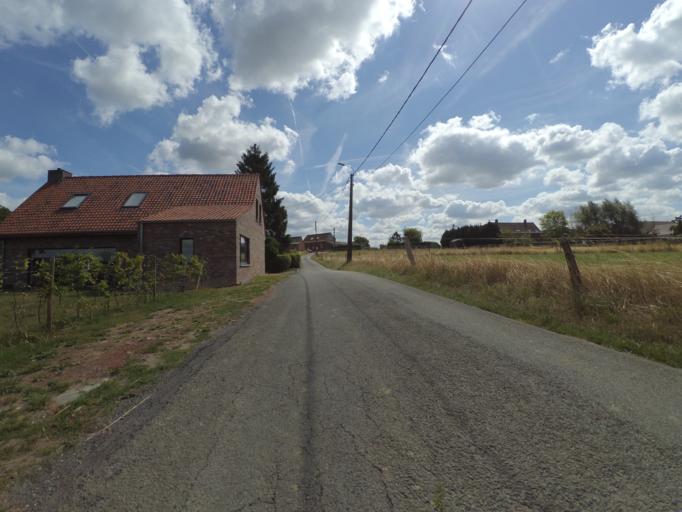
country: BE
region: Wallonia
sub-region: Province du Hainaut
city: Frasnes-lez-Anvaing
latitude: 50.7225
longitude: 3.6397
